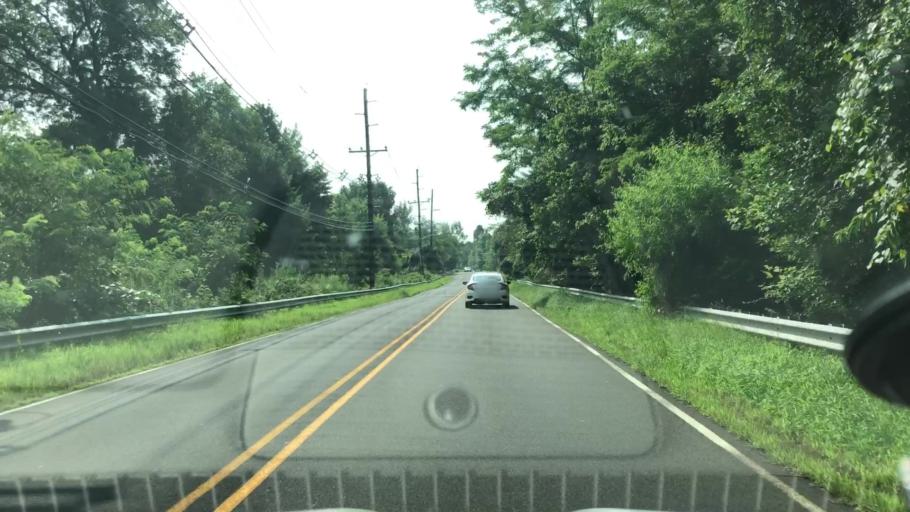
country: US
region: New Jersey
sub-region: Mercer County
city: Lawrenceville
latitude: 40.3038
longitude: -74.6899
